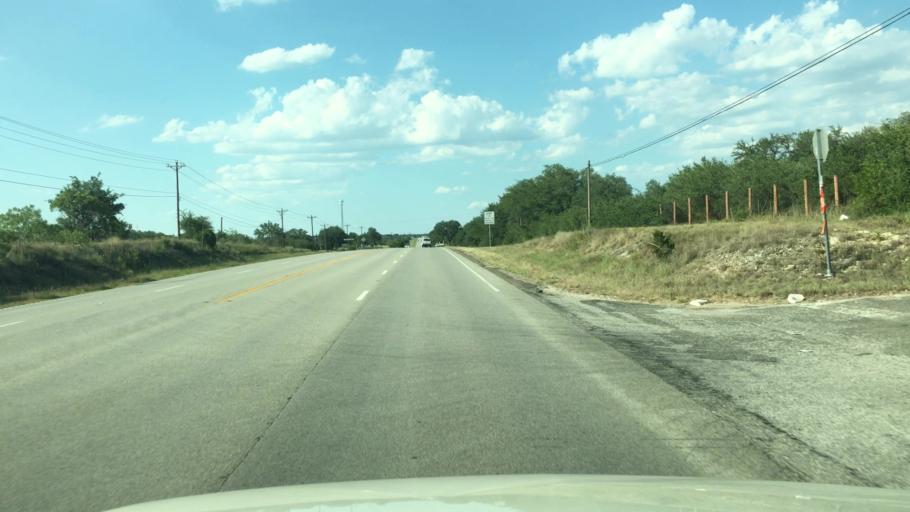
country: US
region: Texas
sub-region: Blanco County
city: Johnson City
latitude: 30.3228
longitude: -98.3885
